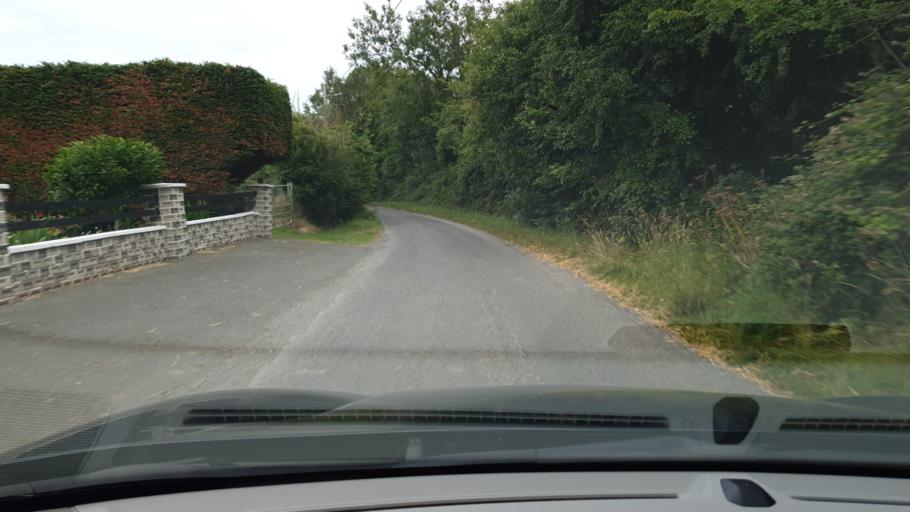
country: IE
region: Leinster
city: Lusk
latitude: 53.5429
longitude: -6.1572
